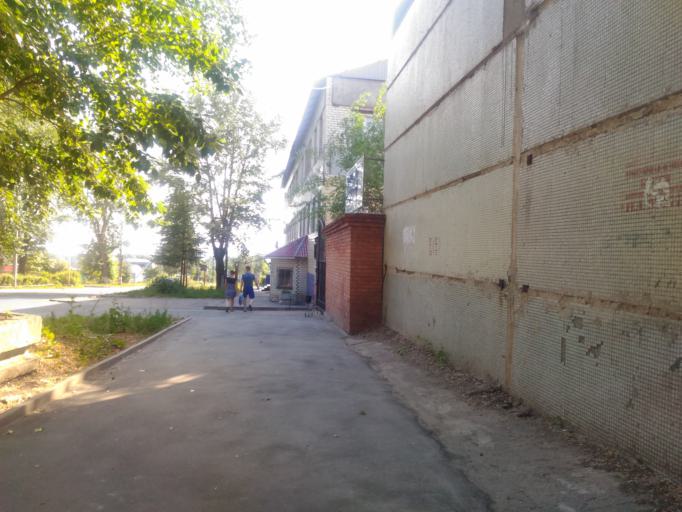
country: RU
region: Ulyanovsk
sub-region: Ulyanovskiy Rayon
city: Ulyanovsk
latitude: 54.3397
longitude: 48.3645
